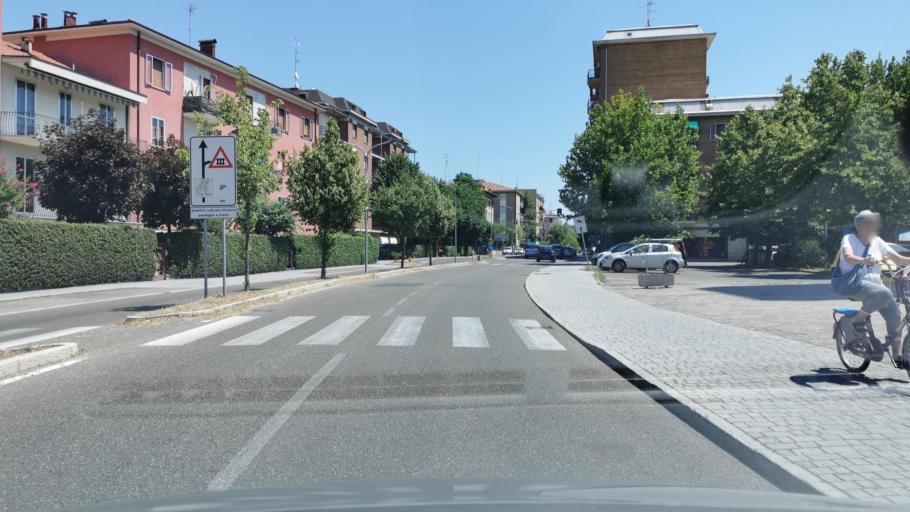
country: IT
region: Emilia-Romagna
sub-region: Provincia di Modena
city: Modena
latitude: 44.6343
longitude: 10.9247
